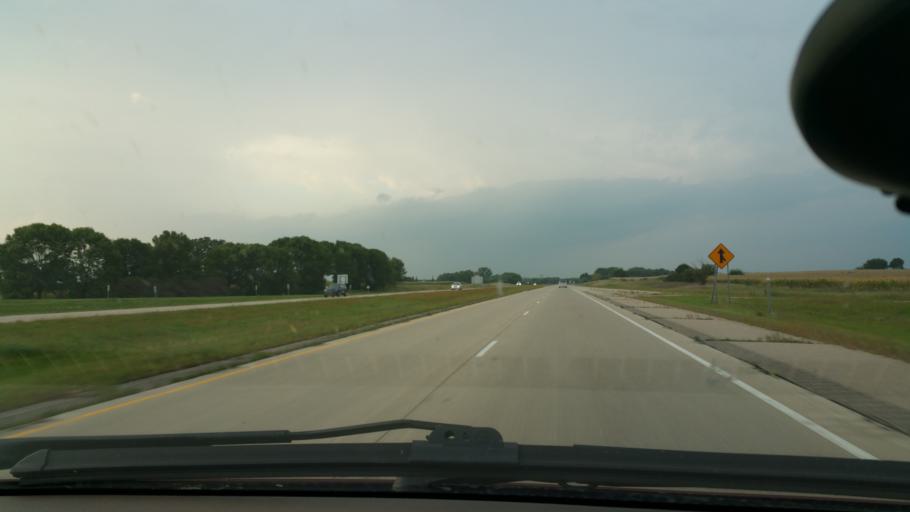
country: US
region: Minnesota
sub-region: Freeborn County
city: Albert Lea
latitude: 43.5765
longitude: -93.3585
